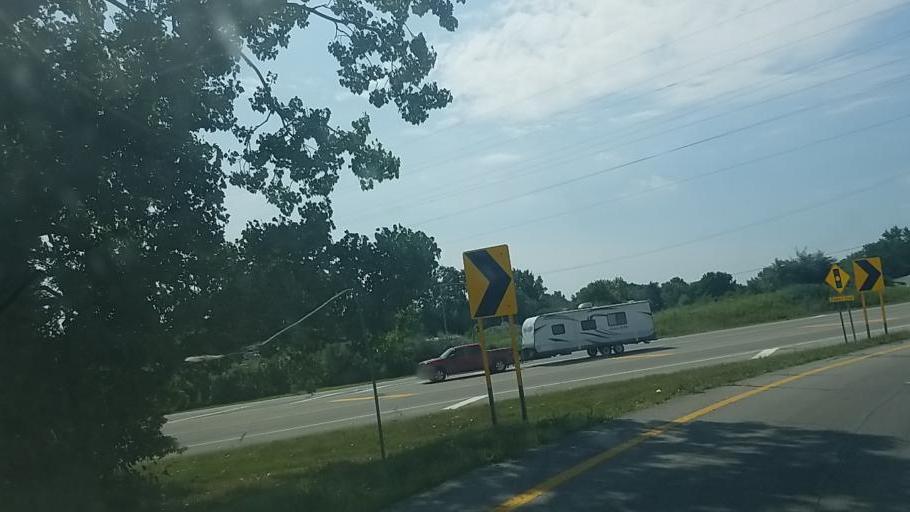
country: US
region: Ohio
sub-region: Richland County
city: Lincoln Heights
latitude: 40.7785
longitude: -82.4724
